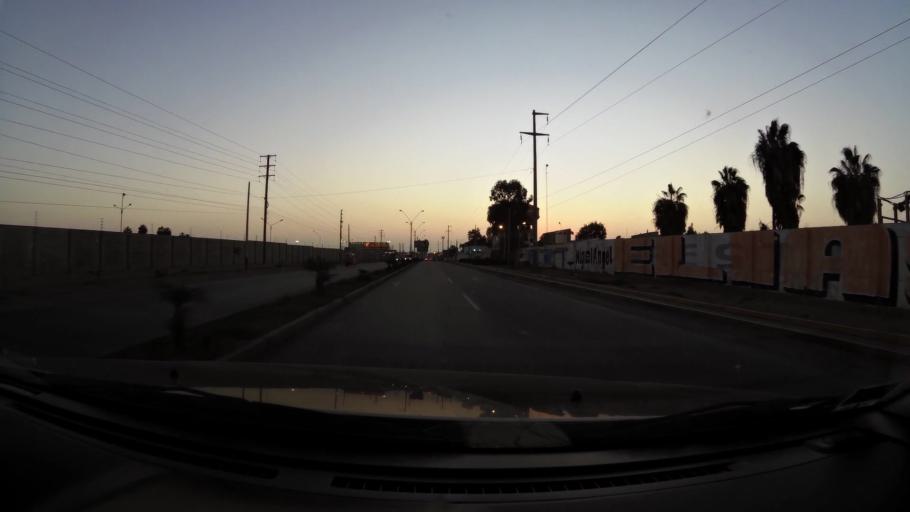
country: PE
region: Ica
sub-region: Provincia de Pisco
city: Pisco
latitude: -13.7111
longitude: -76.1910
